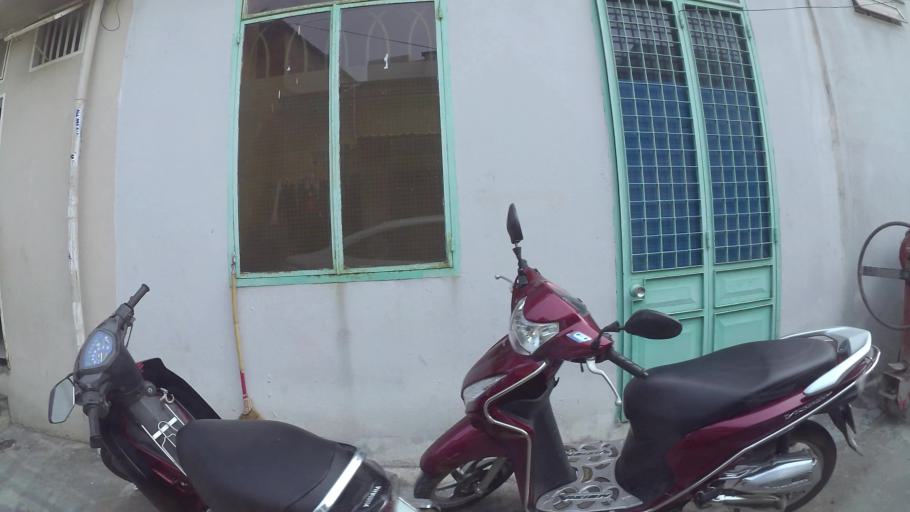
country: VN
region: Da Nang
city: Son Tra
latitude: 16.0411
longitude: 108.2163
